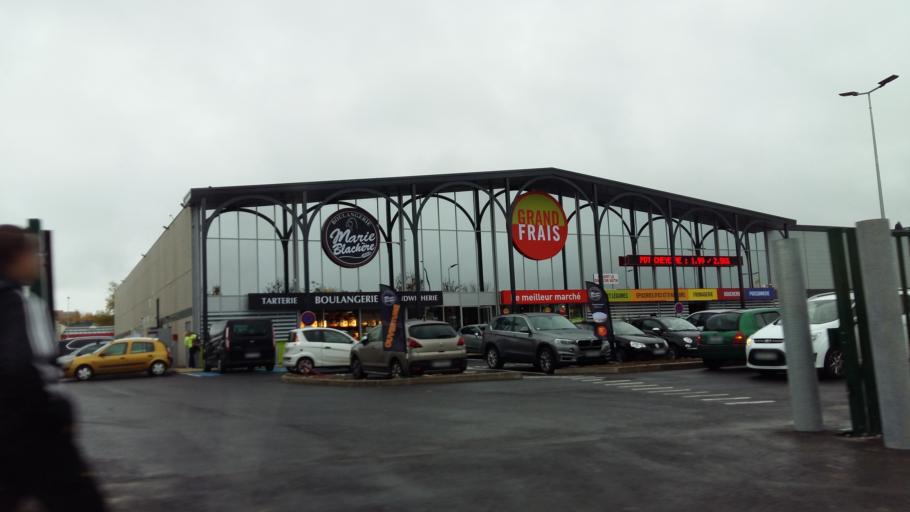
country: FR
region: Ile-de-France
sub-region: Departement des Yvelines
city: Plaisir
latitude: 48.8259
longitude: 1.9679
